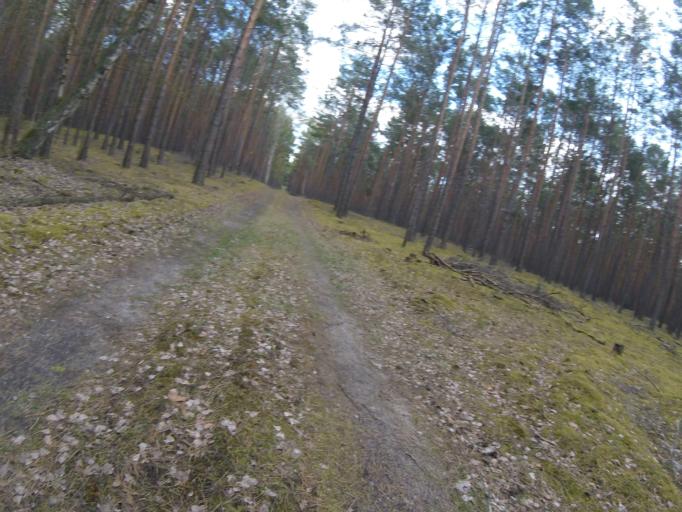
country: DE
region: Brandenburg
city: Halbe
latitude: 52.1826
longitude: 13.7515
